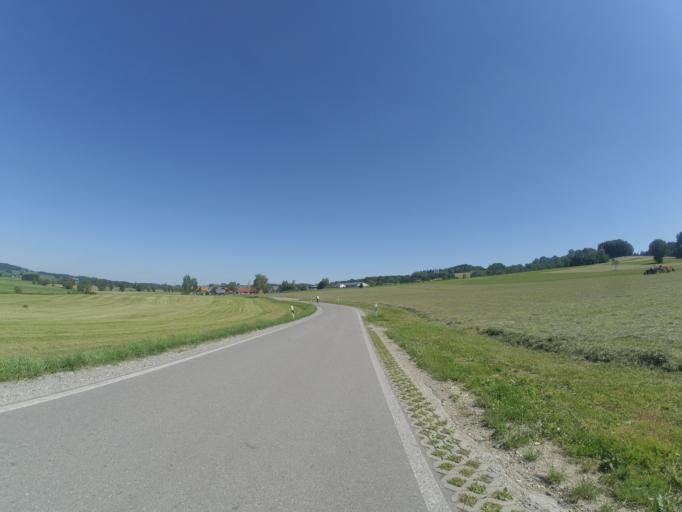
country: DE
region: Baden-Wuerttemberg
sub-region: Tuebingen Region
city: Bad Wurzach
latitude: 47.8622
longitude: 9.9348
